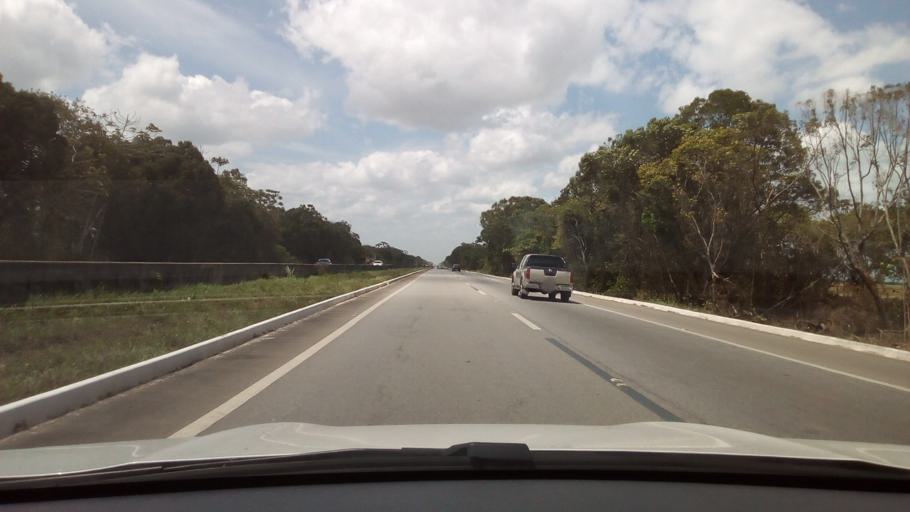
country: BR
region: Paraiba
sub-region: Mamanguape
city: Mamanguape
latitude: -6.9184
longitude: -35.1105
